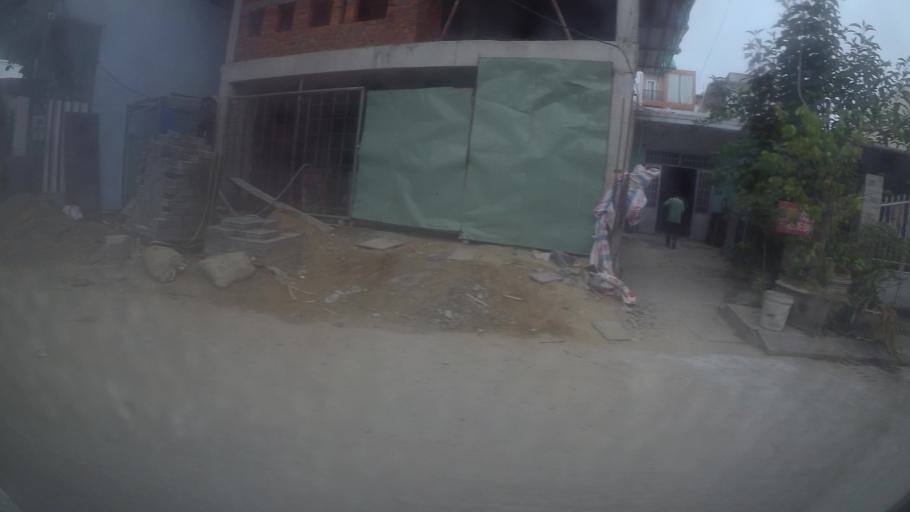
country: VN
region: Da Nang
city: Son Tra
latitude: 16.0423
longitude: 108.2457
